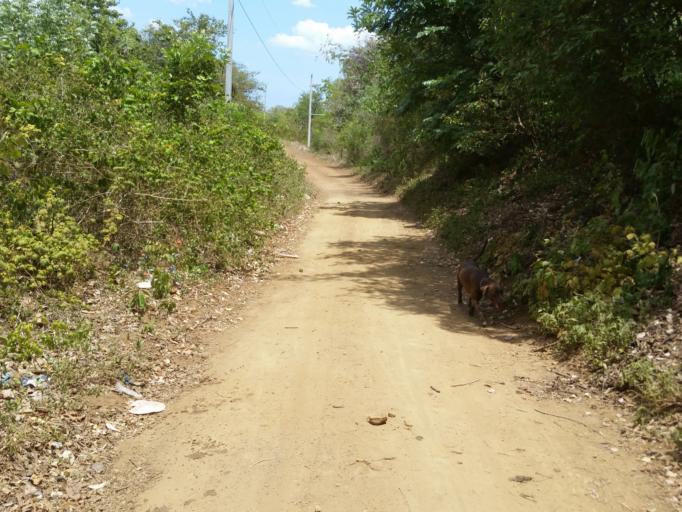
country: NI
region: Managua
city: Carlos Fonseca Amador
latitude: 11.9631
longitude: -86.4283
